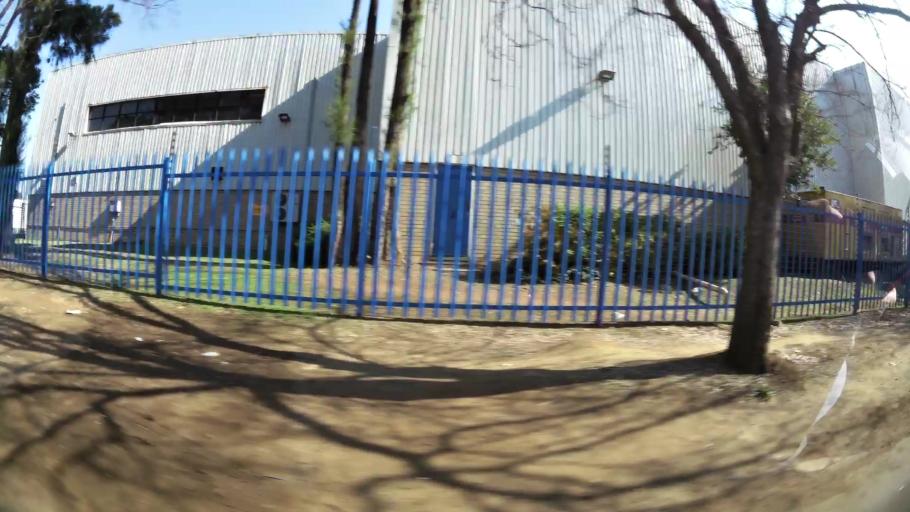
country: ZA
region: Gauteng
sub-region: City of Johannesburg Metropolitan Municipality
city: Modderfontein
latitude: -26.1316
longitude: 28.2170
